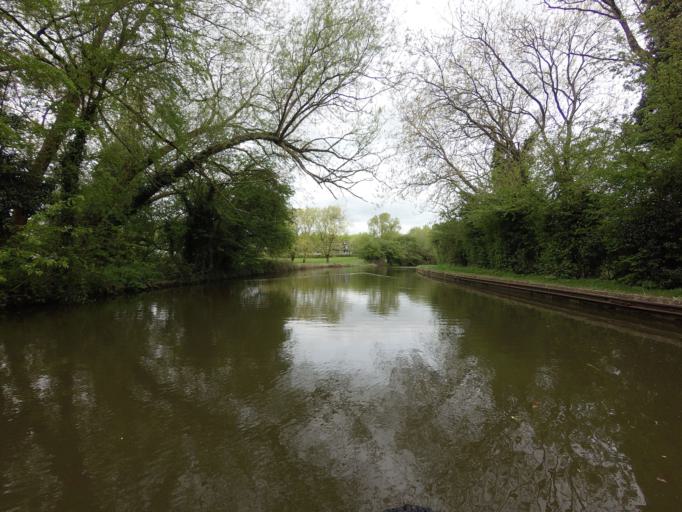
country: GB
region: England
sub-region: Milton Keynes
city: Simpson
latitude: 52.0154
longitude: -0.7200
